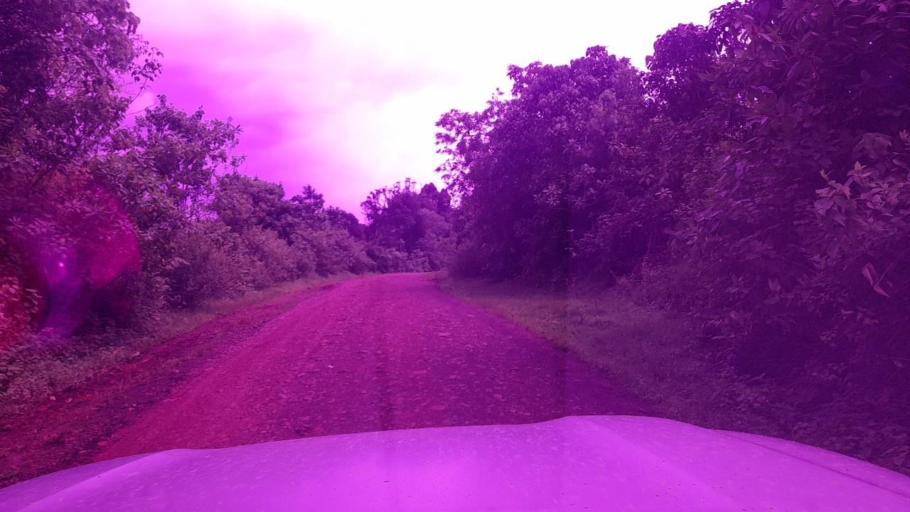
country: ET
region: Southern Nations, Nationalities, and People's Region
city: Tippi
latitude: 7.6291
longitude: 35.5615
